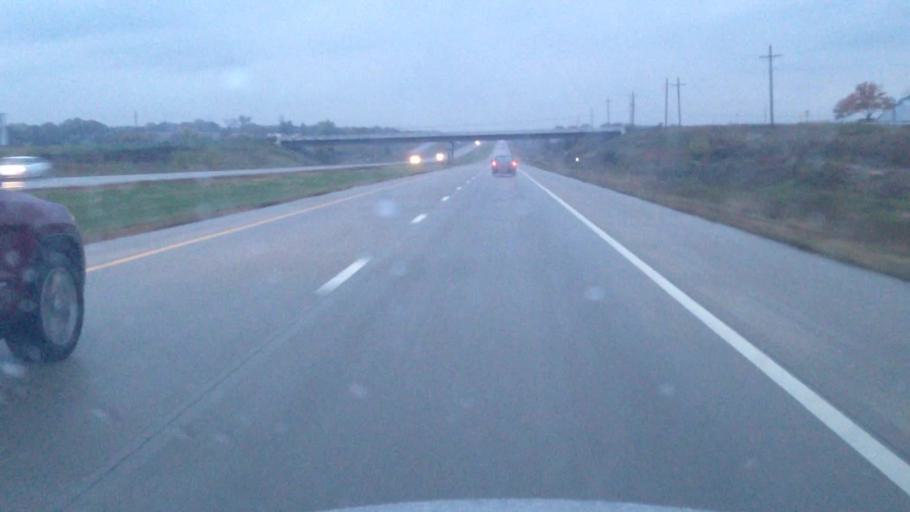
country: US
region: Kansas
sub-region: Douglas County
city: Baldwin City
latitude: 38.8211
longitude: -95.2692
